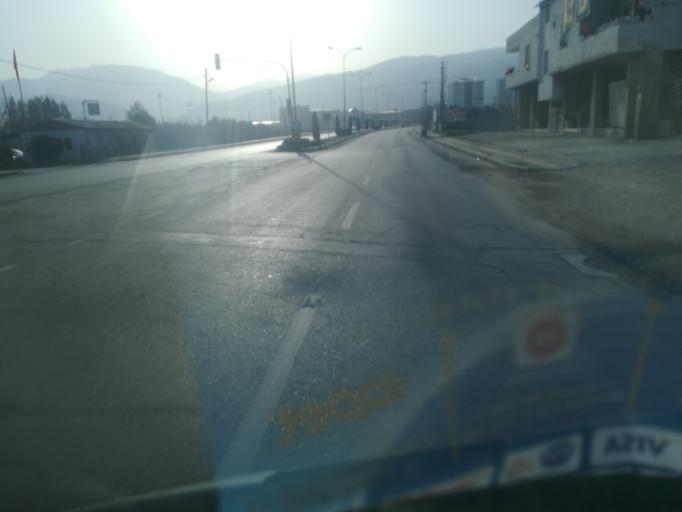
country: TR
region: Osmaniye
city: Osmaniye
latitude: 37.0571
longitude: 36.2196
